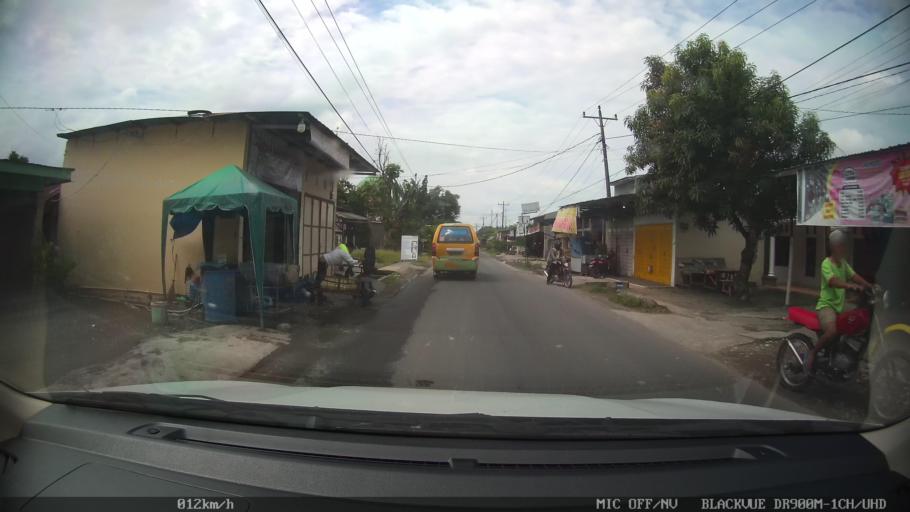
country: ID
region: North Sumatra
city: Sunggal
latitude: 3.6256
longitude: 98.5938
